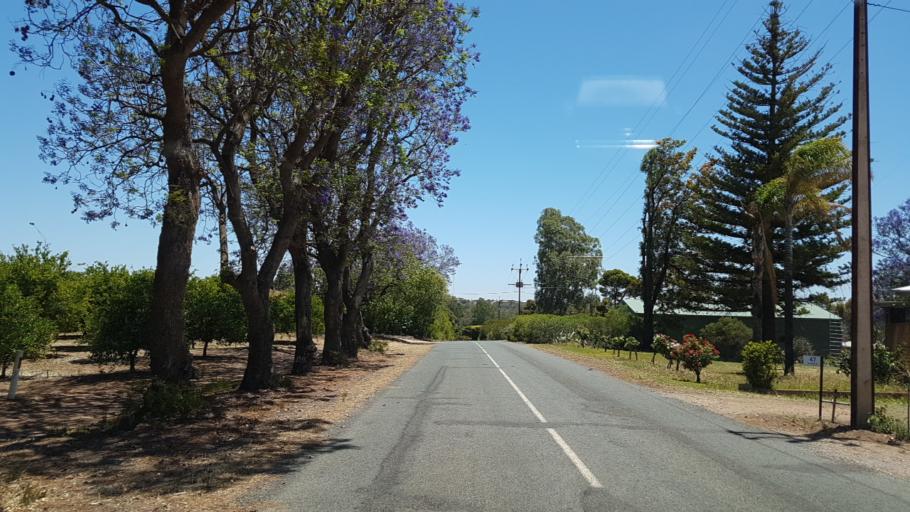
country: AU
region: South Australia
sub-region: Loxton Waikerie
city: Waikerie
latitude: -34.1666
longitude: 140.0359
